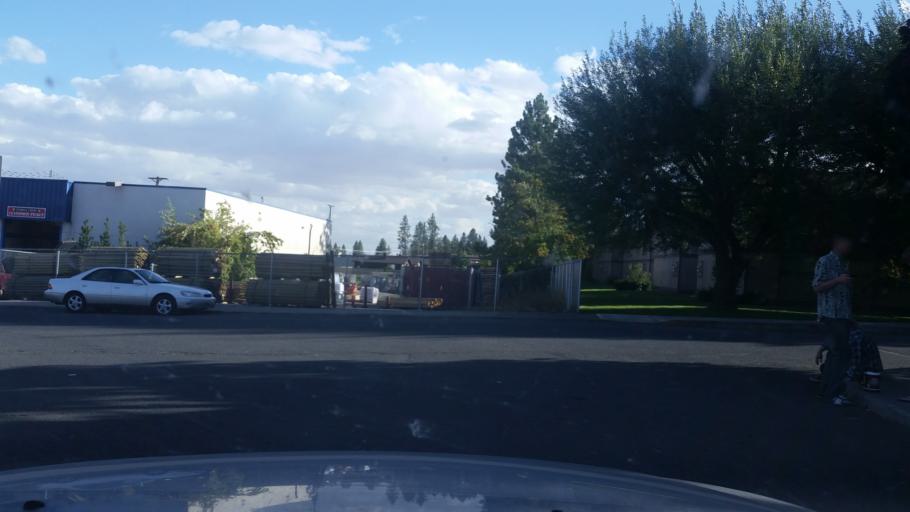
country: US
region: Washington
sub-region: Spokane County
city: Cheney
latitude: 47.5014
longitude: -117.5663
